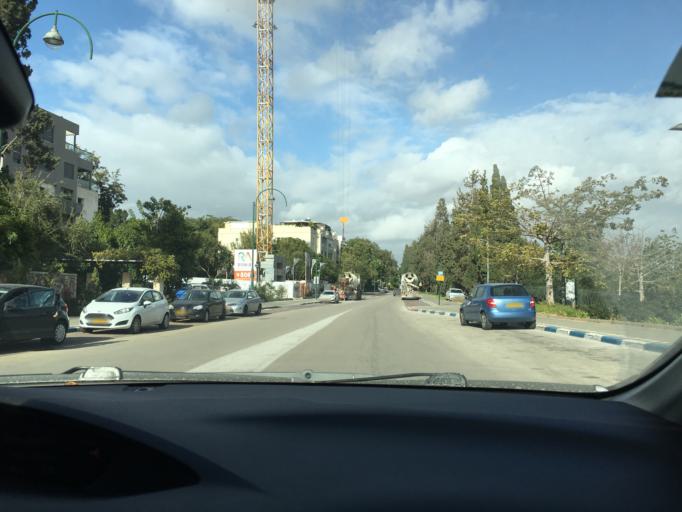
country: IL
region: Tel Aviv
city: Ramat HaSharon
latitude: 32.1411
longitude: 34.8464
